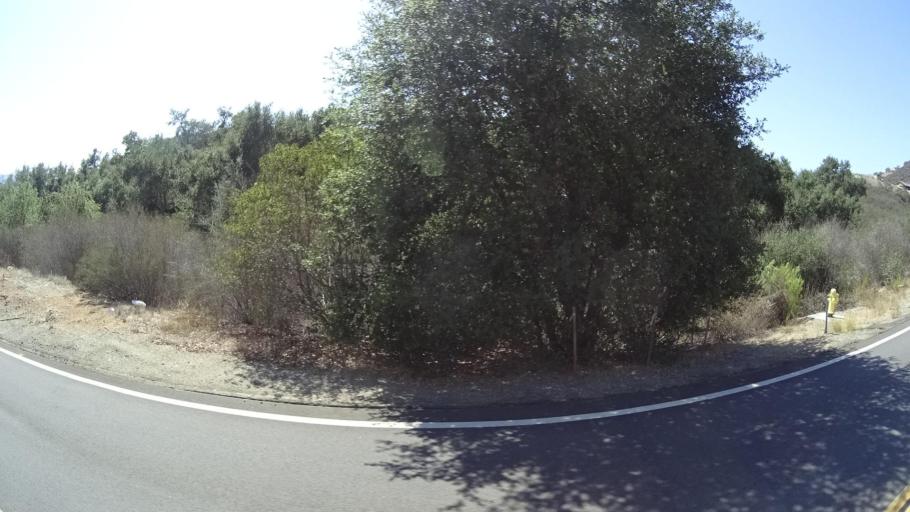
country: US
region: California
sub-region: San Diego County
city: Harbison Canyon
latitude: 32.8264
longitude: -116.8345
